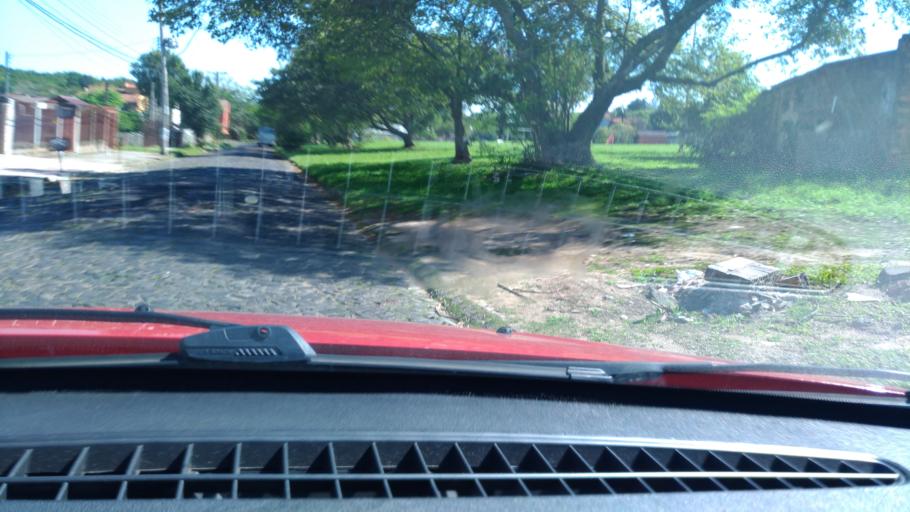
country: BR
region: Rio Grande do Sul
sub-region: Cachoeirinha
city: Cachoeirinha
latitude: -30.0335
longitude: -51.1269
